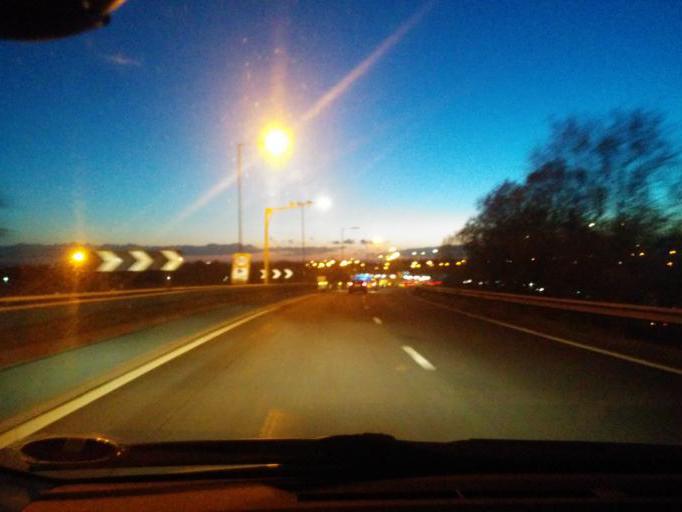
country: GB
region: England
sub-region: Borough of Bolton
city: Kearsley
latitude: 53.5223
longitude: -2.3624
